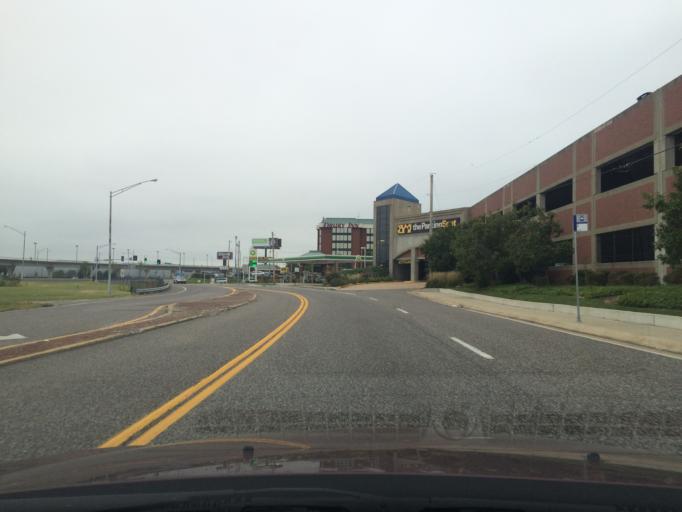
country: US
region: Missouri
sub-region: Saint Louis County
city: Woodson Terrace
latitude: 38.7382
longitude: -90.3663
